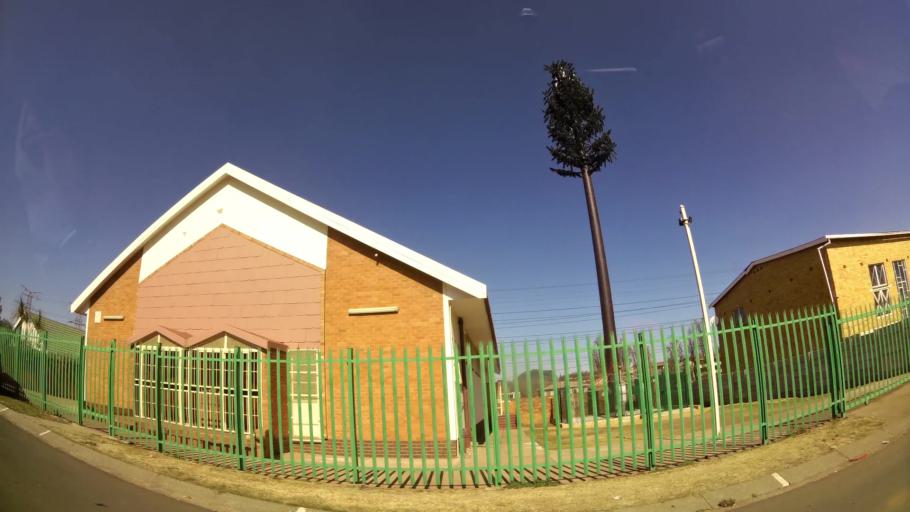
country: ZA
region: Gauteng
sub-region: City of Johannesburg Metropolitan Municipality
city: Johannesburg
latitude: -26.1905
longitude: 27.9618
